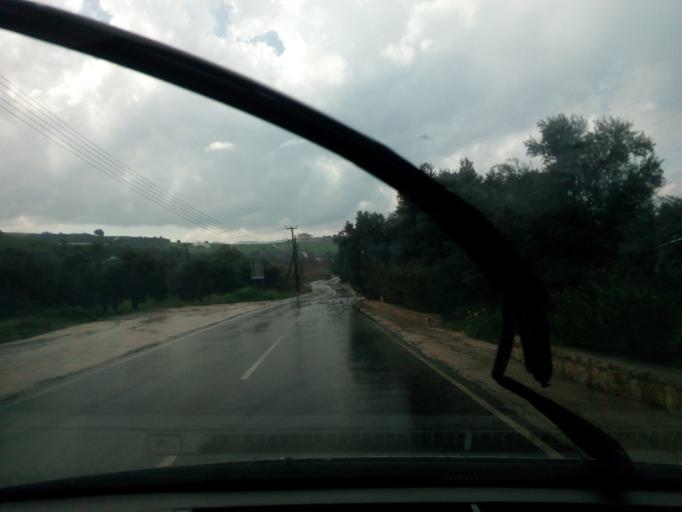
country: CY
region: Pafos
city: Polis
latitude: 35.0024
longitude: 32.4670
